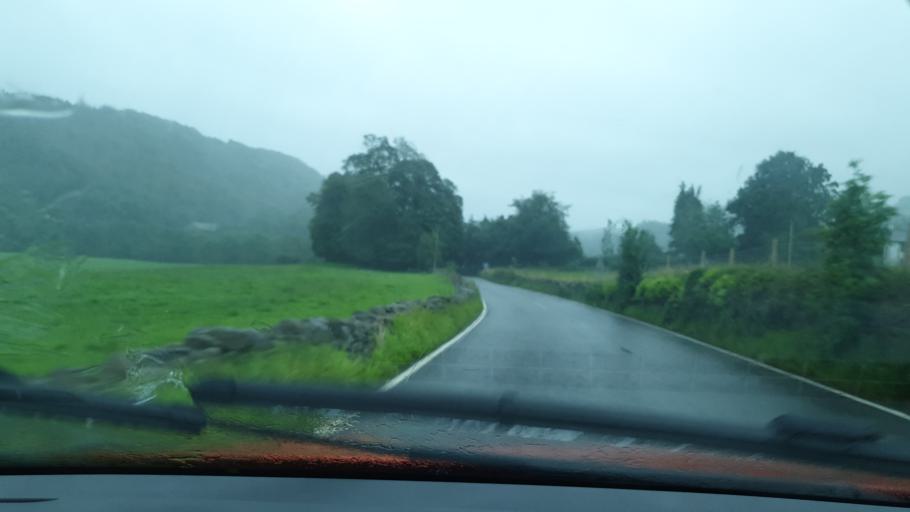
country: GB
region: England
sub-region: Cumbria
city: Ulverston
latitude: 54.2484
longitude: -3.0679
